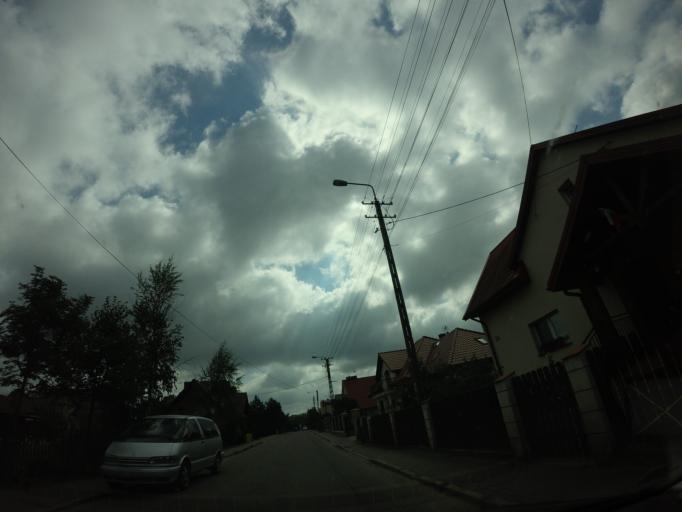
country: PL
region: Podlasie
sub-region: Bialystok
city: Bialystok
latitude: 53.1230
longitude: 23.2311
